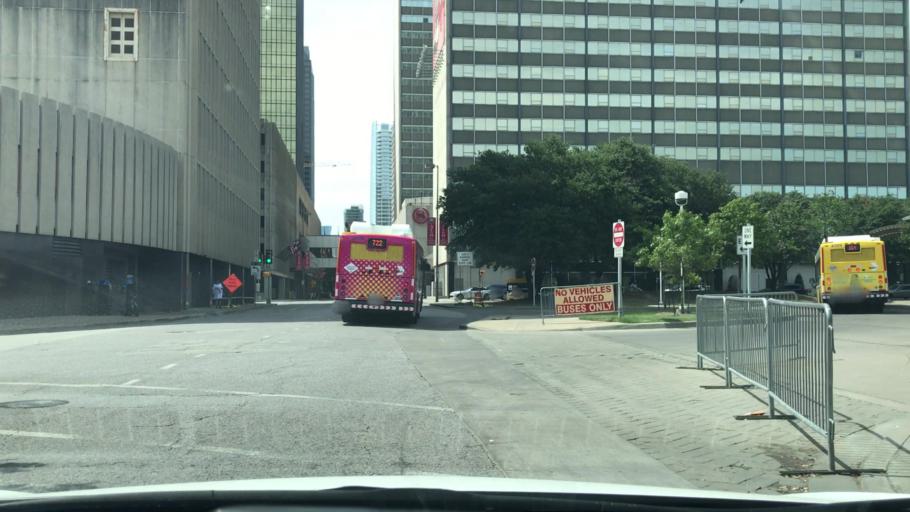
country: US
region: Texas
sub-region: Dallas County
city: Dallas
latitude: 32.7837
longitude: -96.7938
